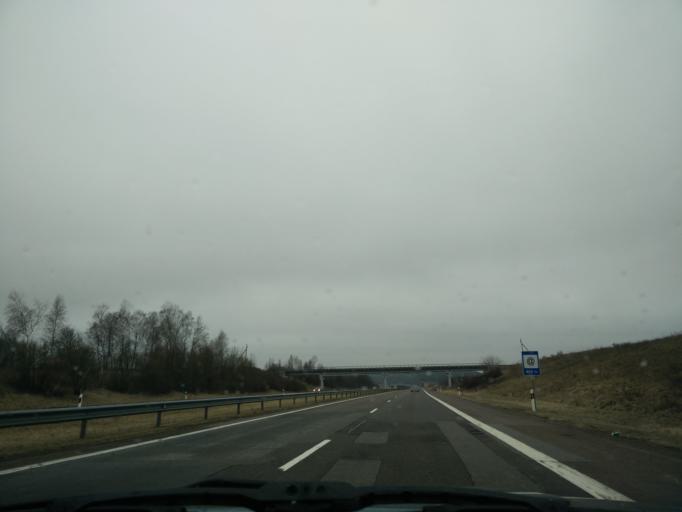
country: LT
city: Skaudvile
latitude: 55.4068
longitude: 22.8409
